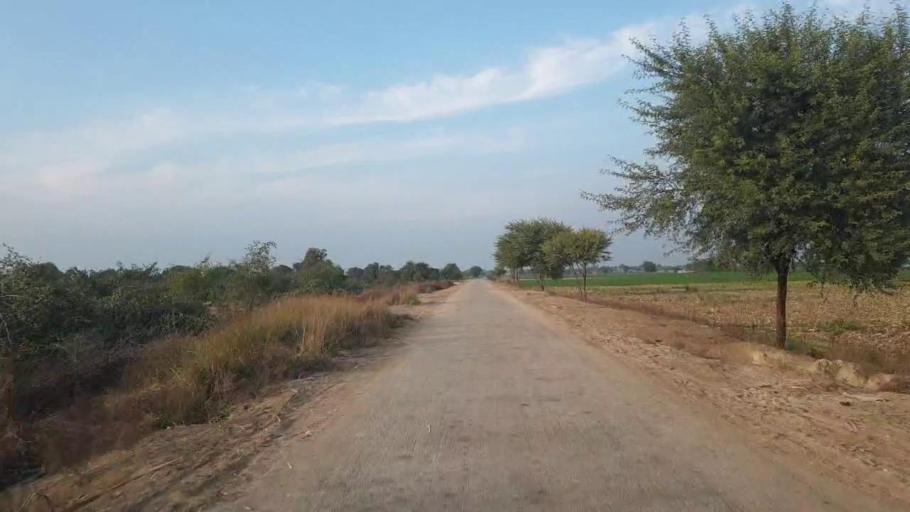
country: PK
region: Sindh
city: Shahpur Chakar
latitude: 26.1113
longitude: 68.5465
